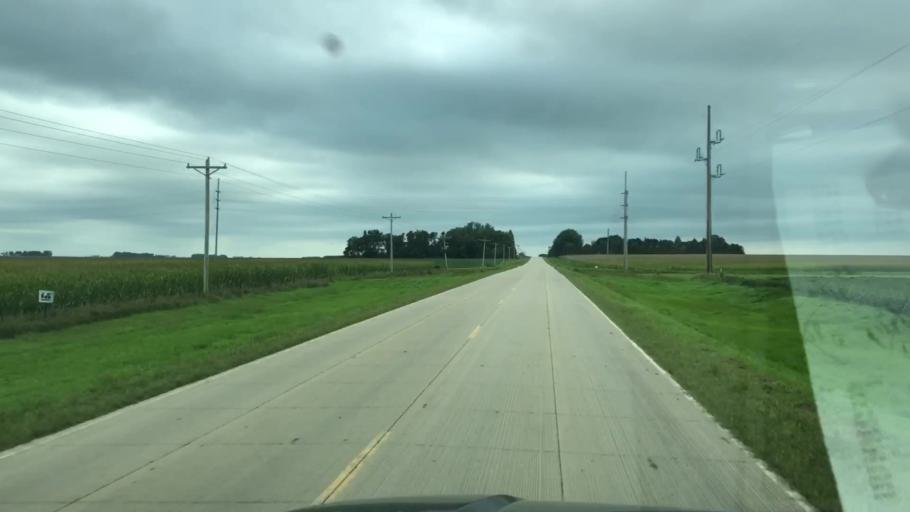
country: US
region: Iowa
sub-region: O'Brien County
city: Sheldon
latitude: 43.1735
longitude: -95.9801
